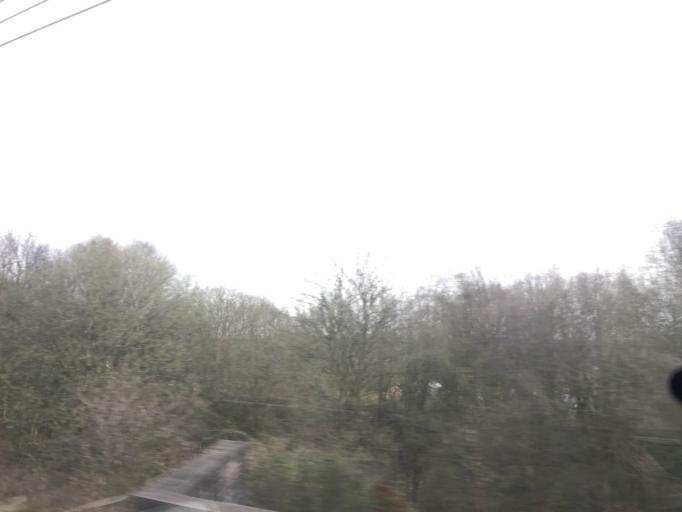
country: GB
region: England
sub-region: Lancashire
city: Adlington
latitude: 53.5833
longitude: -2.6409
